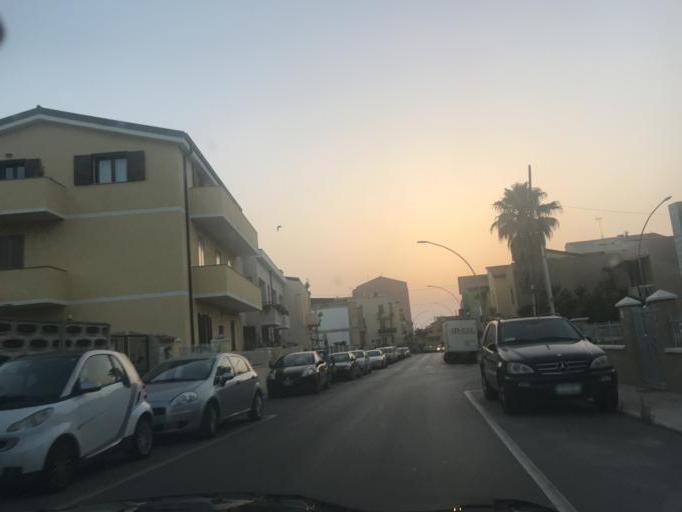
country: IT
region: Sardinia
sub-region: Provincia di Sassari
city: Alghero
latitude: 40.5560
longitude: 8.3287
